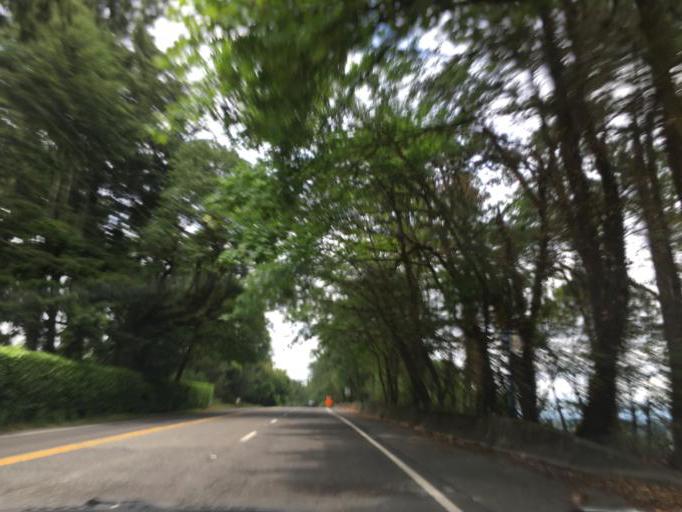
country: US
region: Oregon
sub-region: Clackamas County
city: Milwaukie
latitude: 45.4357
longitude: -122.6536
